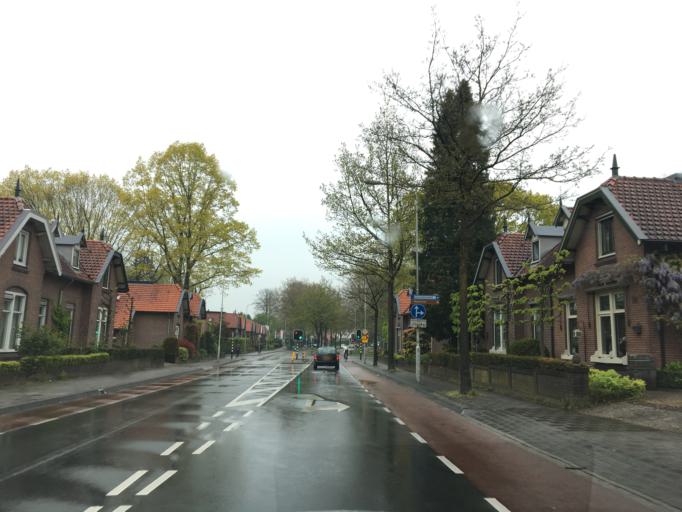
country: NL
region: Gelderland
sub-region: Gemeente Ede
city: Ede
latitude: 52.0362
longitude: 5.6713
